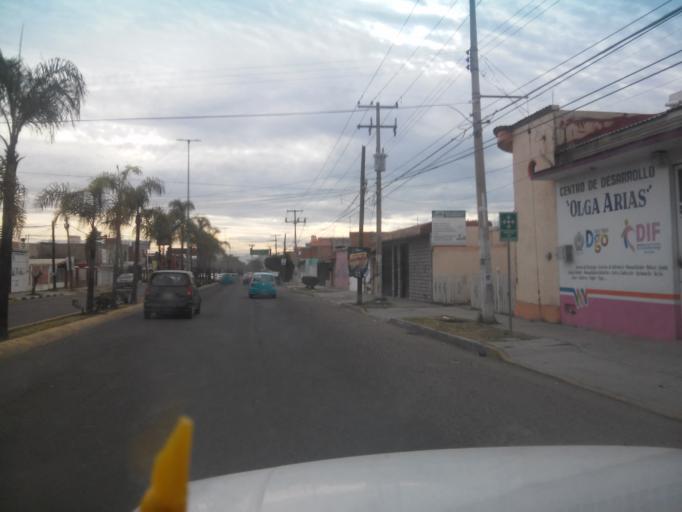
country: MX
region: Durango
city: Victoria de Durango
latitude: 24.0103
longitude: -104.6668
